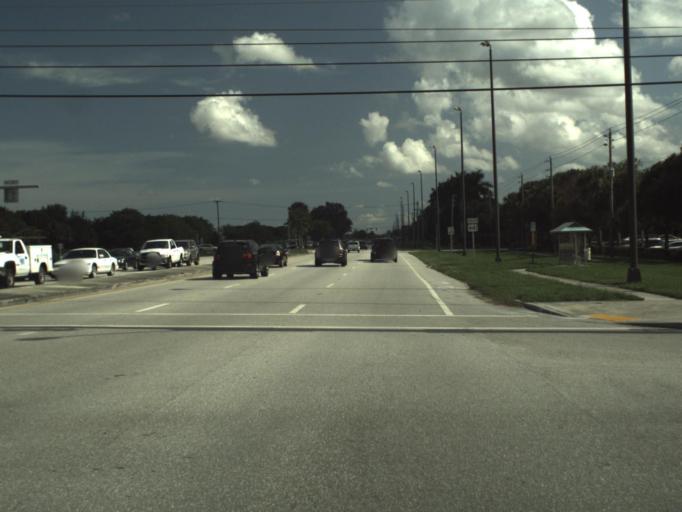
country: US
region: Florida
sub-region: Palm Beach County
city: Boca Pointe
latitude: 26.3496
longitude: -80.2035
